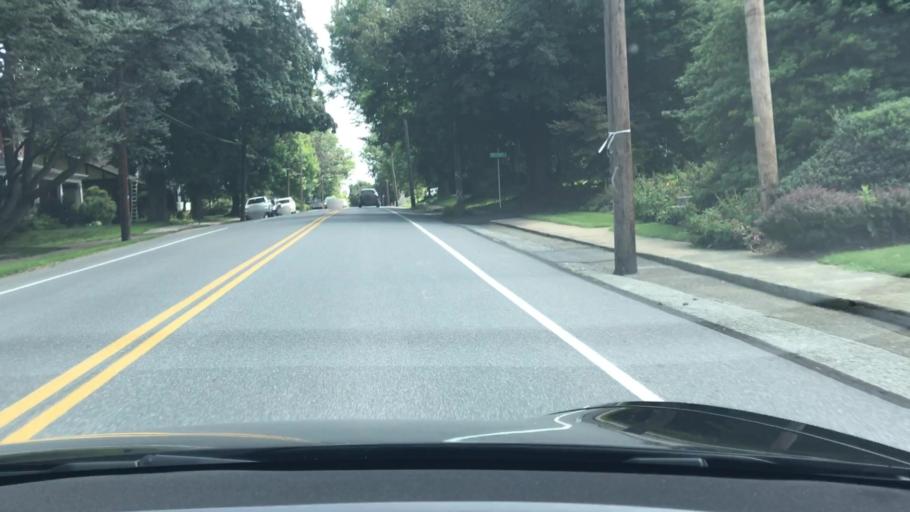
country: US
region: Pennsylvania
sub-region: Lancaster County
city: Salunga
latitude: 40.0989
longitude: -76.4202
